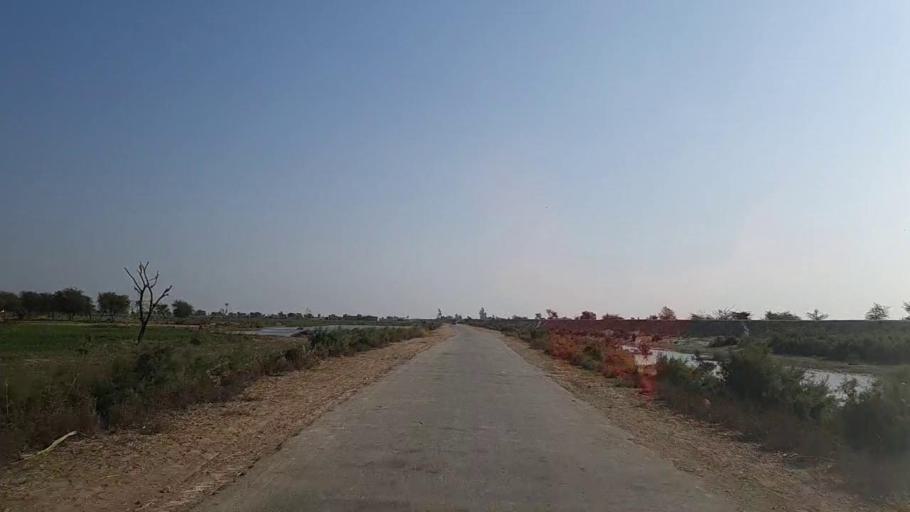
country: PK
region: Sindh
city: Sanghar
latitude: 25.9603
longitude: 69.0395
